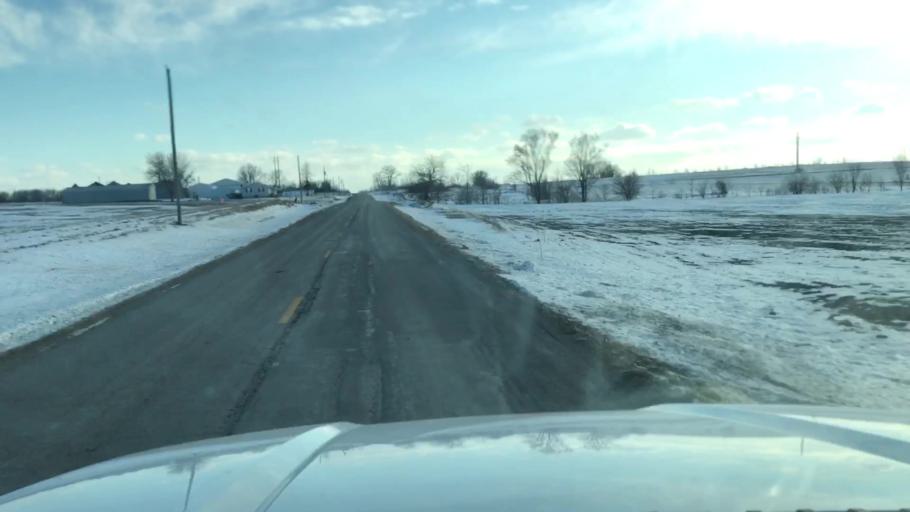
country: US
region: Missouri
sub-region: Holt County
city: Oregon
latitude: 40.1167
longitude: -95.0226
